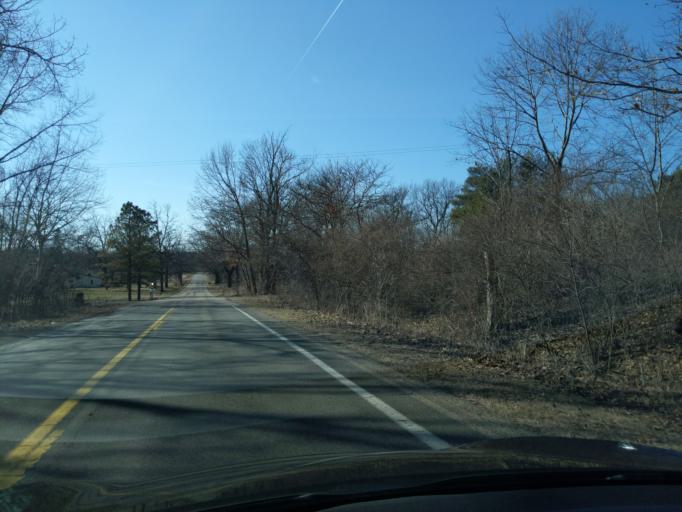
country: US
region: Michigan
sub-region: Ingham County
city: Leslie
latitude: 42.4115
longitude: -84.4318
